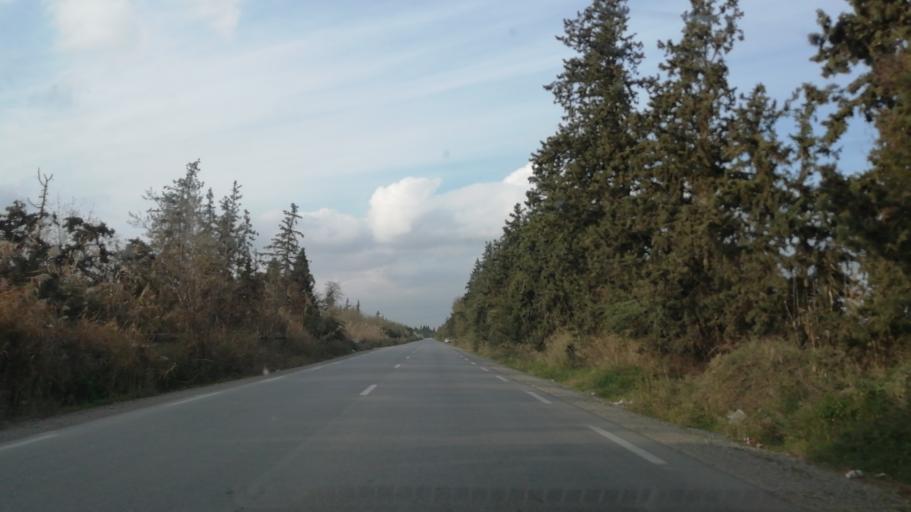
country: DZ
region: Mascara
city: Mascara
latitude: 35.6251
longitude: 0.0437
